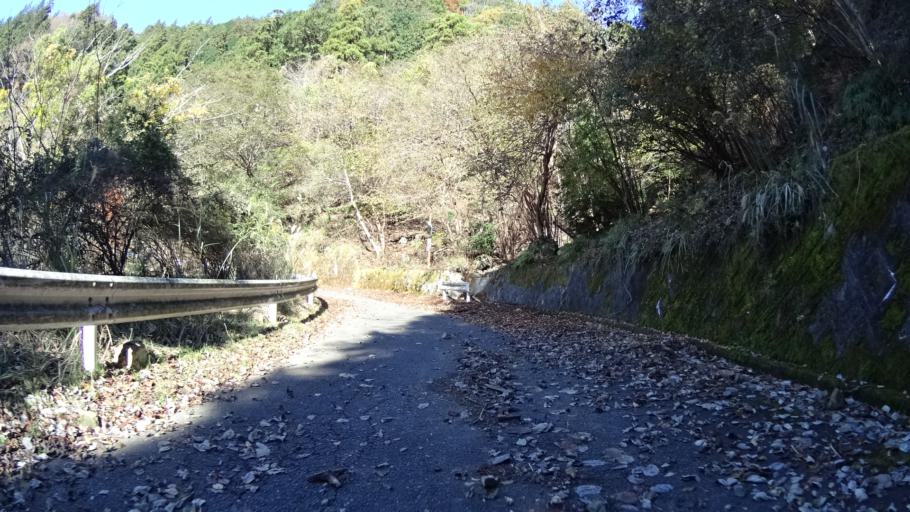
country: JP
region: Kanagawa
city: Atsugi
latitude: 35.5040
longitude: 139.2758
